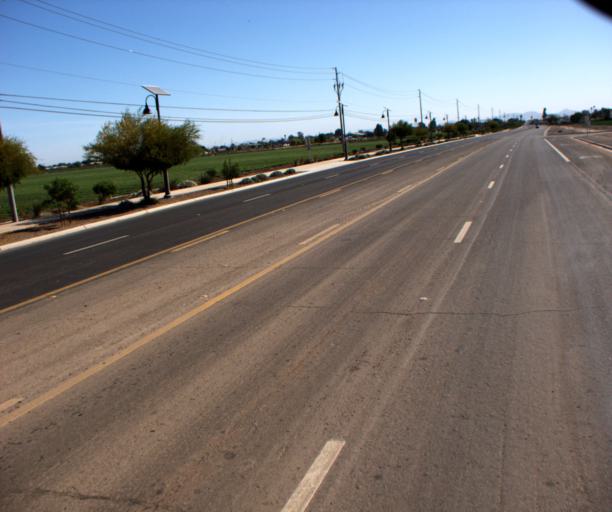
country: US
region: Arizona
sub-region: Yuma County
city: Somerton
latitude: 32.5967
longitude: -114.7262
